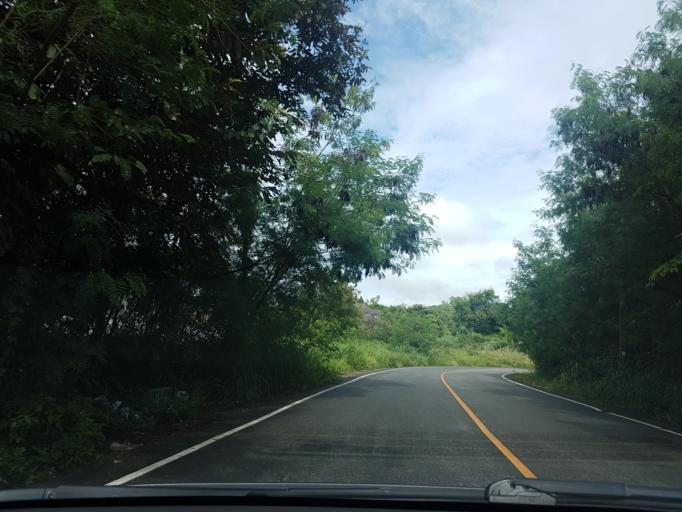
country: TH
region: Chiang Mai
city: San Sai
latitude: 18.8364
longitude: 99.0090
